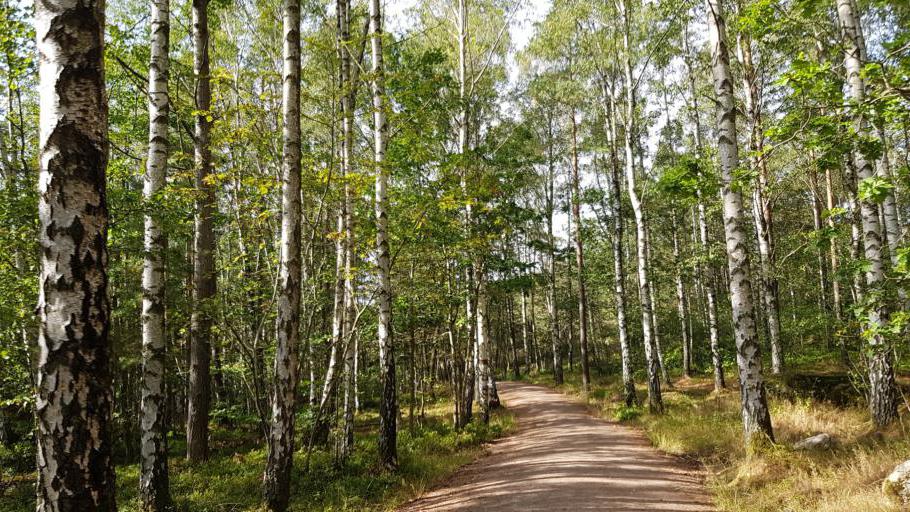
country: SE
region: Vaestra Goetaland
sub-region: Molndal
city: Moelndal
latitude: 57.6917
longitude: 12.0415
